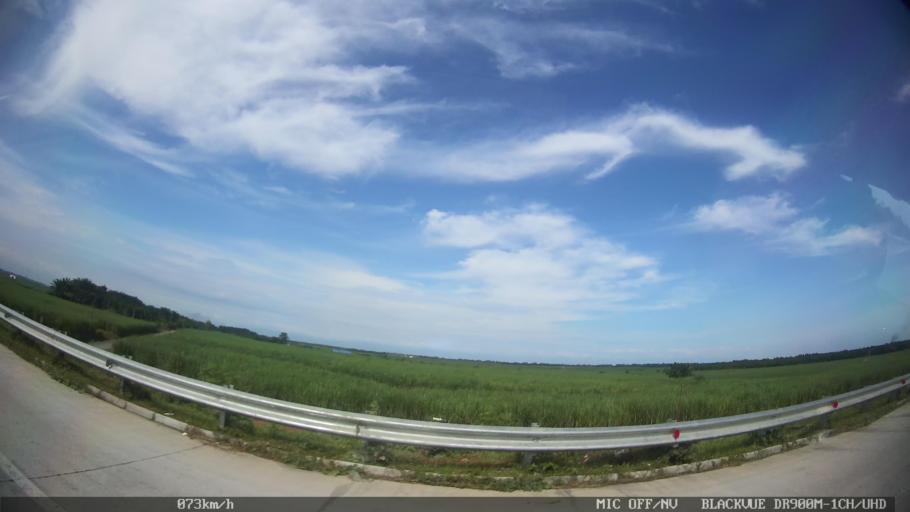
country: ID
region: North Sumatra
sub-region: Kabupaten Langkat
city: Stabat
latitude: 3.7220
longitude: 98.4933
